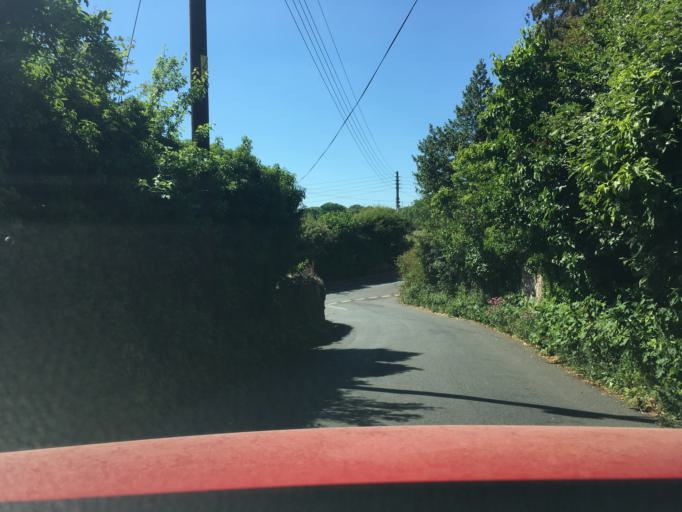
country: GB
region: England
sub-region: South Gloucestershire
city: Winterbourne
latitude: 51.5138
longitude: -2.5056
